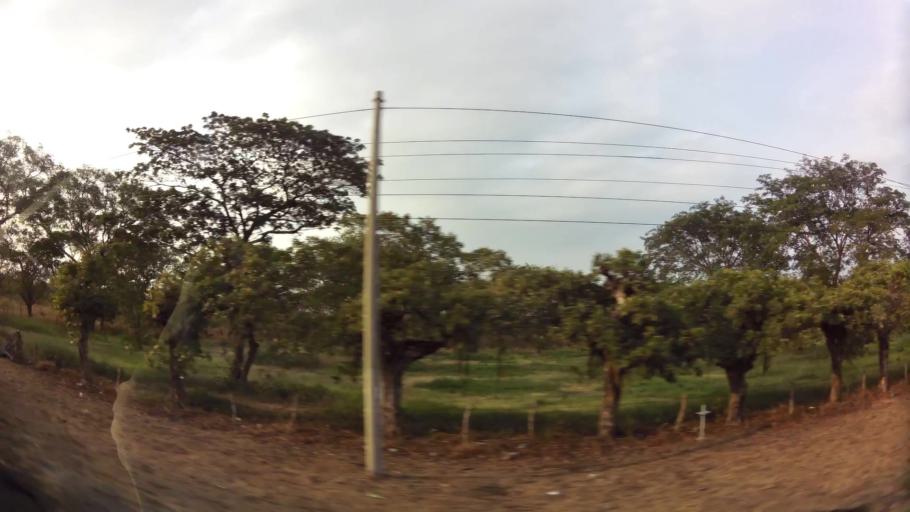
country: NI
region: Leon
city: Nagarote
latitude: 12.2733
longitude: -86.4915
